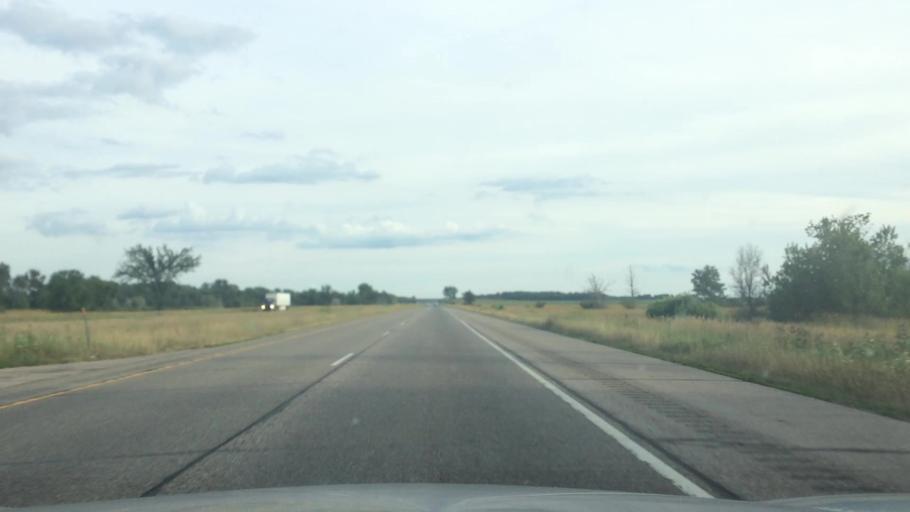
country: US
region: Wisconsin
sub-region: Waushara County
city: Wautoma
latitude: 44.1657
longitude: -89.5327
